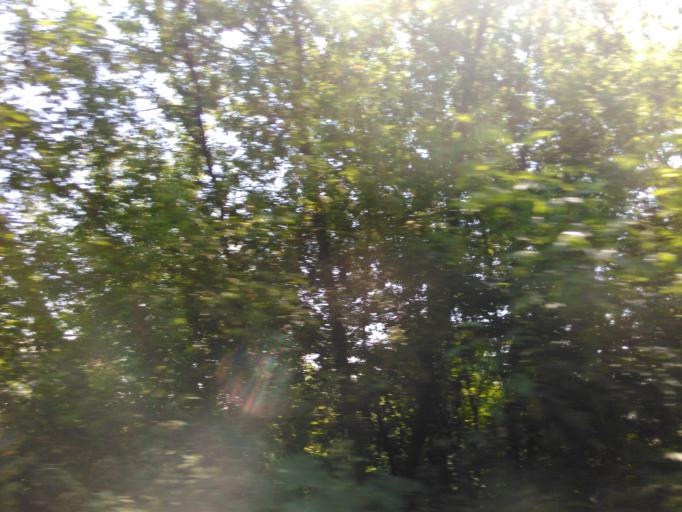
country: RU
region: Moskovskaya
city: Staraya Kupavna
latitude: 55.8012
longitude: 38.1474
